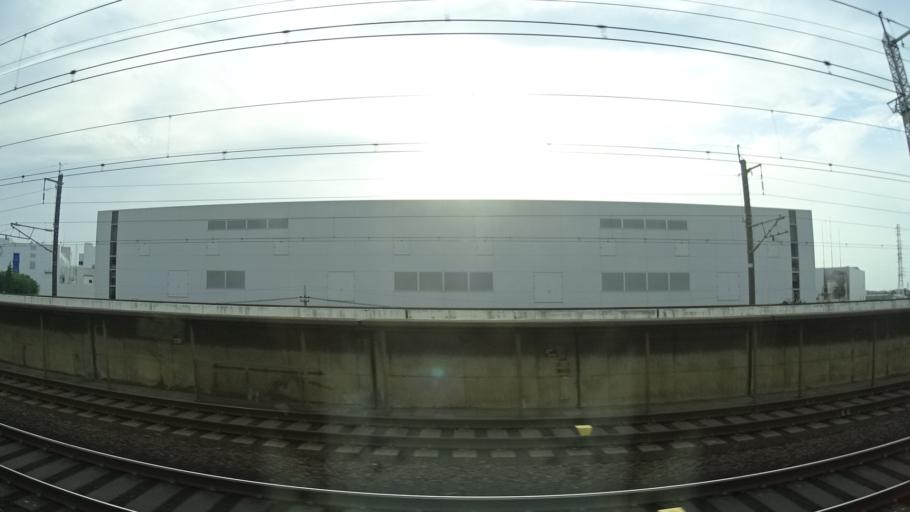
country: JP
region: Saitama
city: Ageoshimo
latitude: 35.9569
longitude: 139.6211
